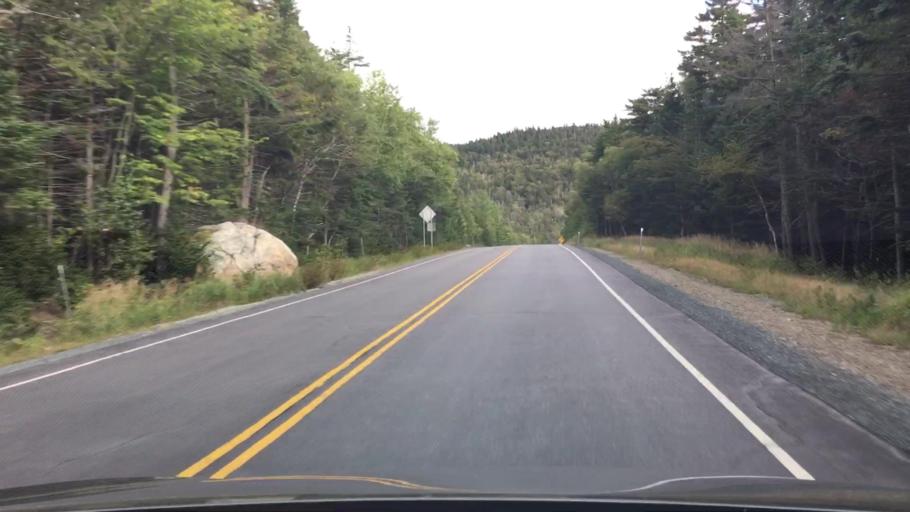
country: US
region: New Hampshire
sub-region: Grafton County
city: Woodstock
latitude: 44.0371
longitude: -71.4999
